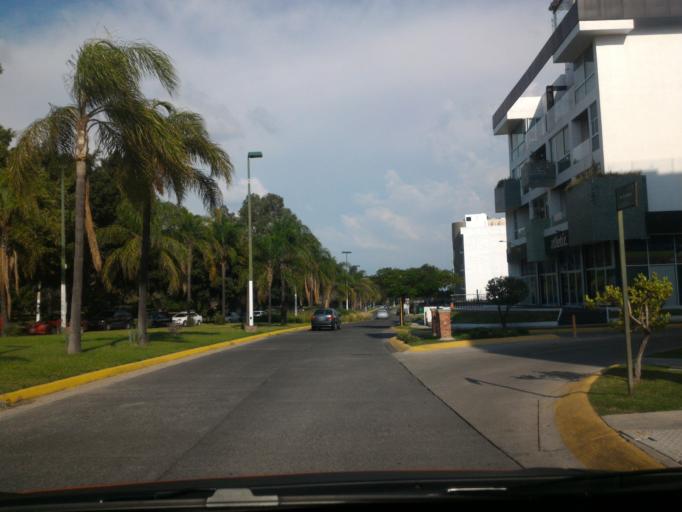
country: MX
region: Jalisco
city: Guadalajara
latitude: 20.6637
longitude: -103.4443
